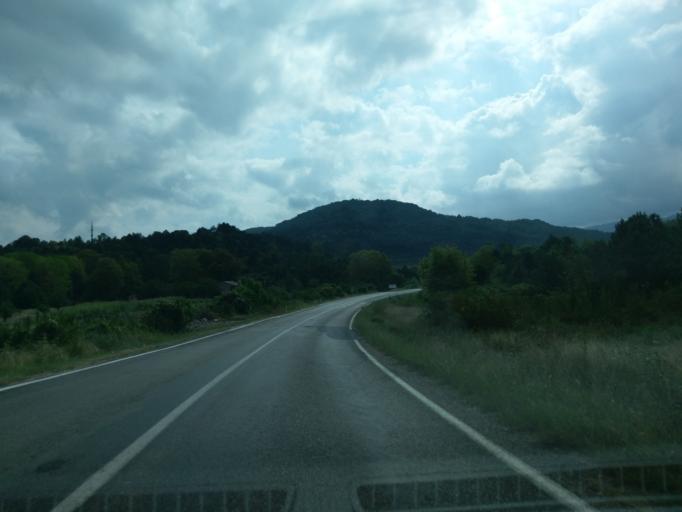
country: TR
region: Sinop
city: Yenikonak
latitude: 41.9415
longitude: 34.7173
